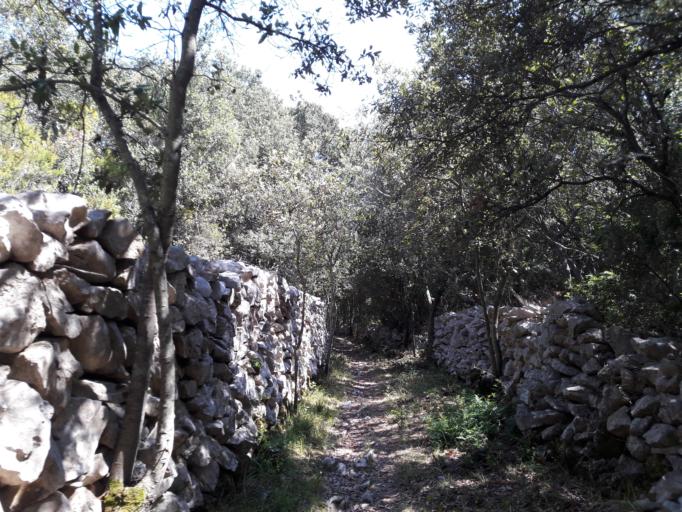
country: HR
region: Licko-Senjska
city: Novalja
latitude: 44.3631
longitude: 14.6962
